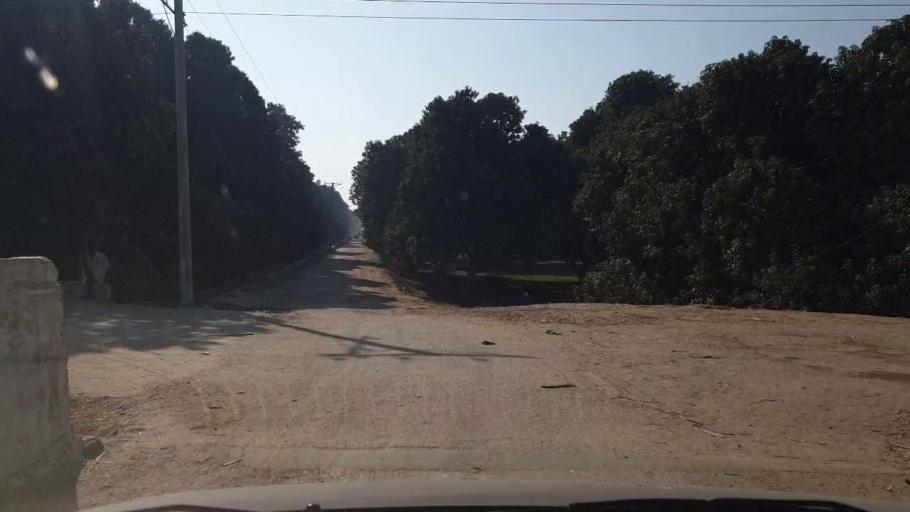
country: PK
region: Sindh
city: Tando Jam
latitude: 25.4447
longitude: 68.5999
